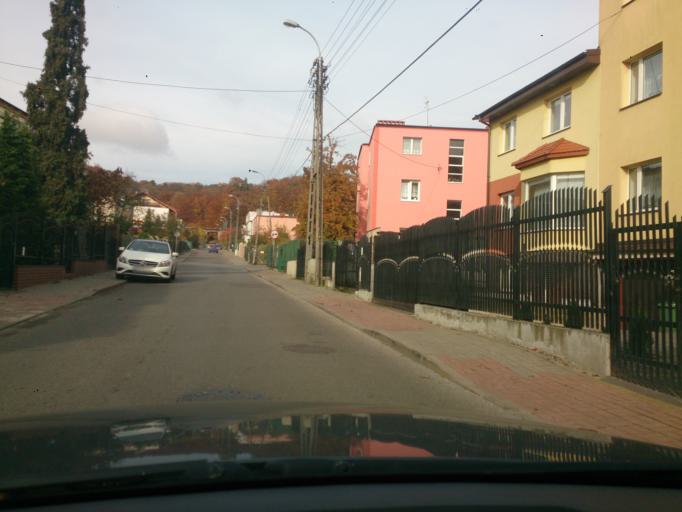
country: PL
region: Pomeranian Voivodeship
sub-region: Gdynia
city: Gdynia
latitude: 54.4859
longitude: 18.5250
